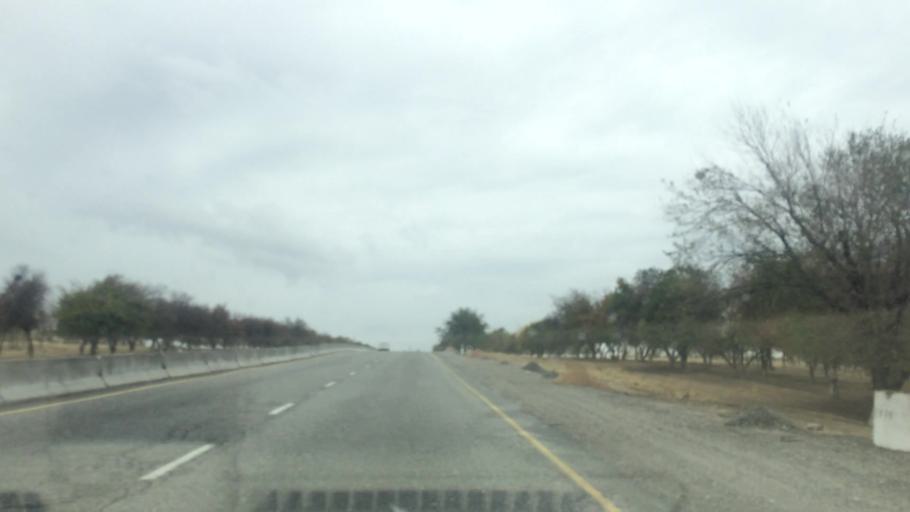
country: UZ
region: Samarqand
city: Bulung'ur
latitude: 39.8598
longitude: 67.4695
